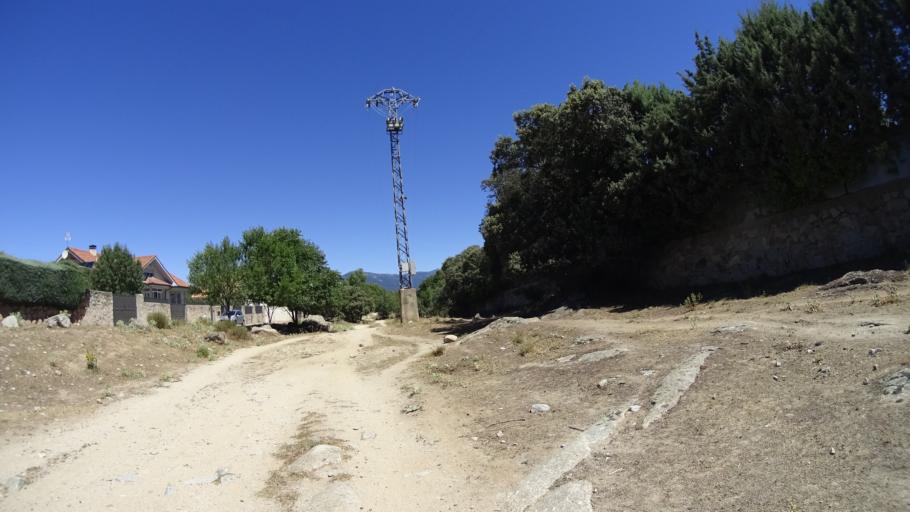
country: ES
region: Madrid
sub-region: Provincia de Madrid
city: Alpedrete
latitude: 40.6563
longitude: -4.0471
